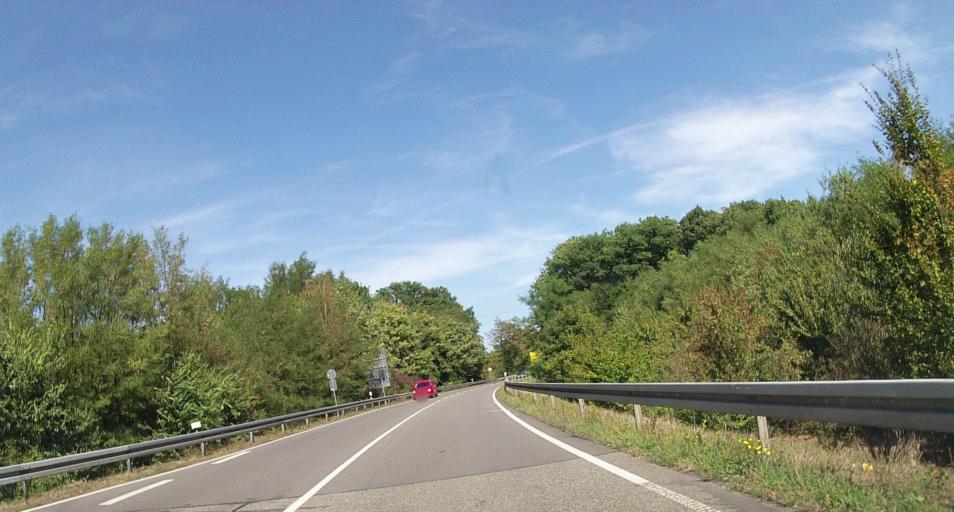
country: DE
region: Baden-Wuerttemberg
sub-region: Karlsruhe Region
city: Rastatt
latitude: 48.8321
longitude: 8.1984
